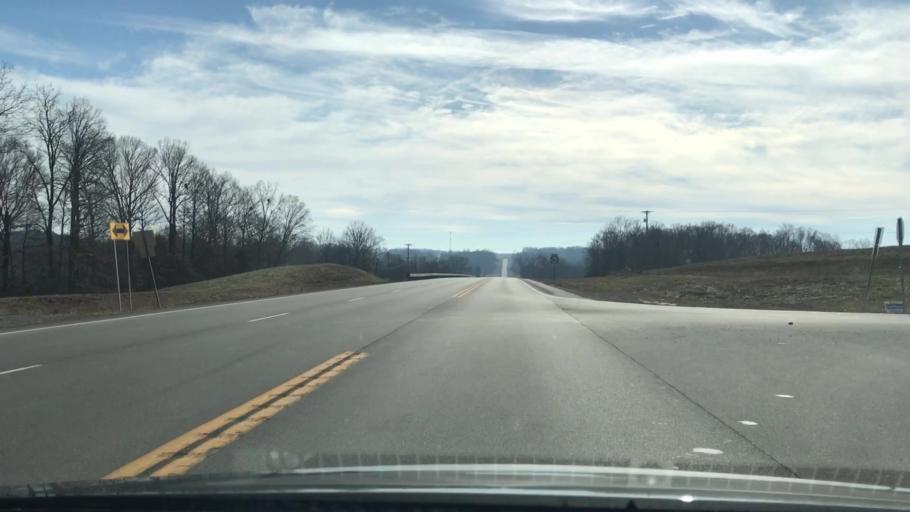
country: US
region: Kentucky
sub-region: Monroe County
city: Tompkinsville
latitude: 36.8155
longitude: -85.6883
